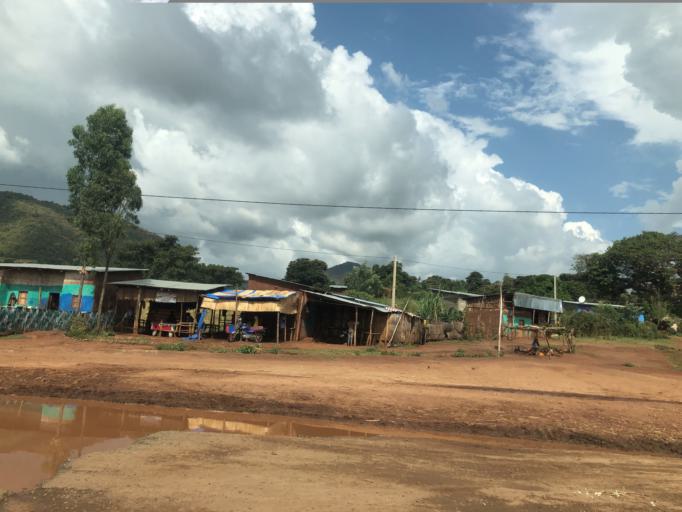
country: ET
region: Southern Nations, Nationalities, and People's Region
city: Bako
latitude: 5.7378
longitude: 36.6088
